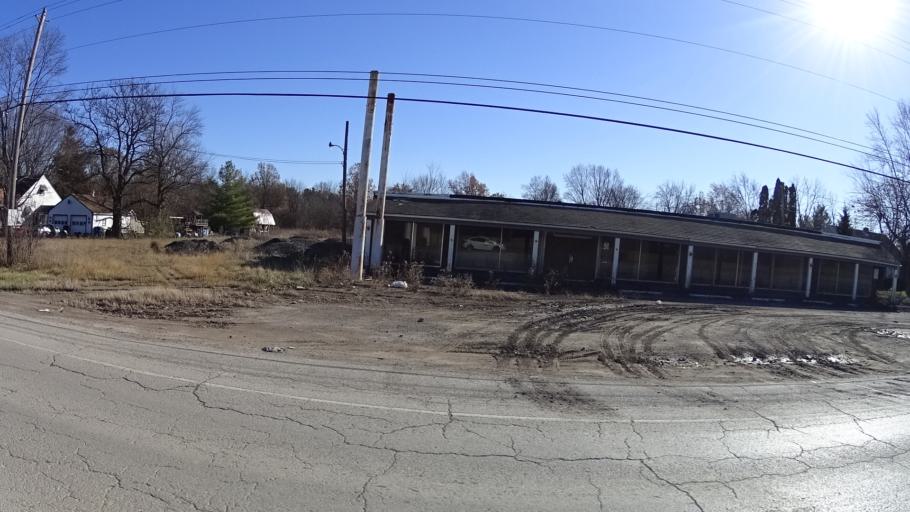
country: US
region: Ohio
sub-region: Lorain County
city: Oberlin
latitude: 41.2978
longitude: -82.1650
